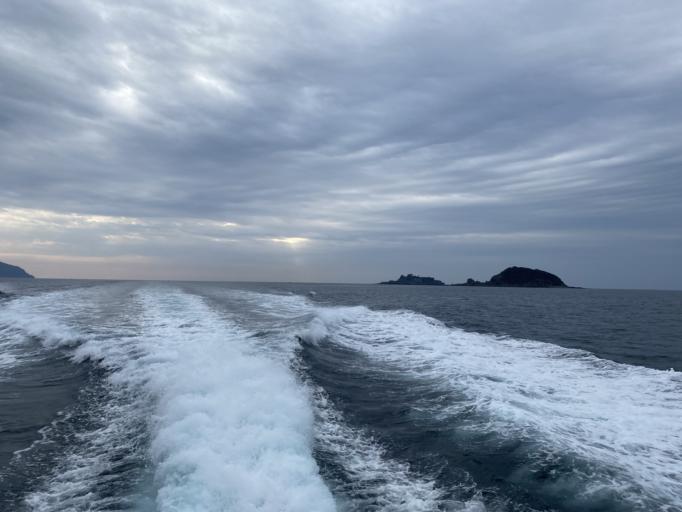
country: JP
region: Nagasaki
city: Nagasaki-shi
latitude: 32.6400
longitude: 129.7617
